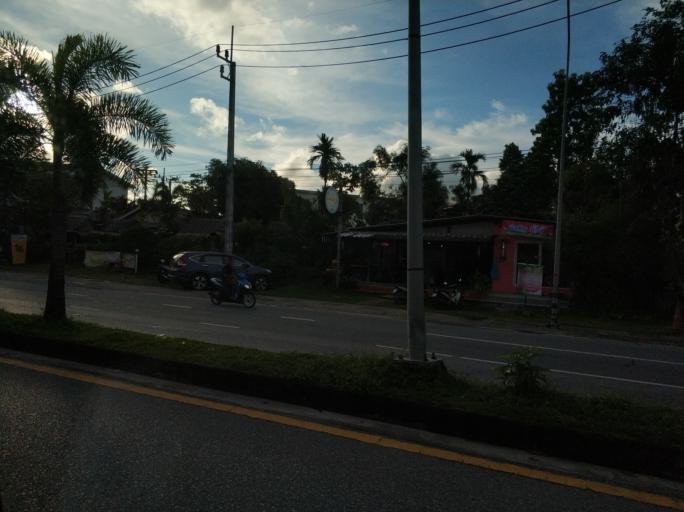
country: TH
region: Phuket
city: Kathu
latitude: 7.8997
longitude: 98.3533
